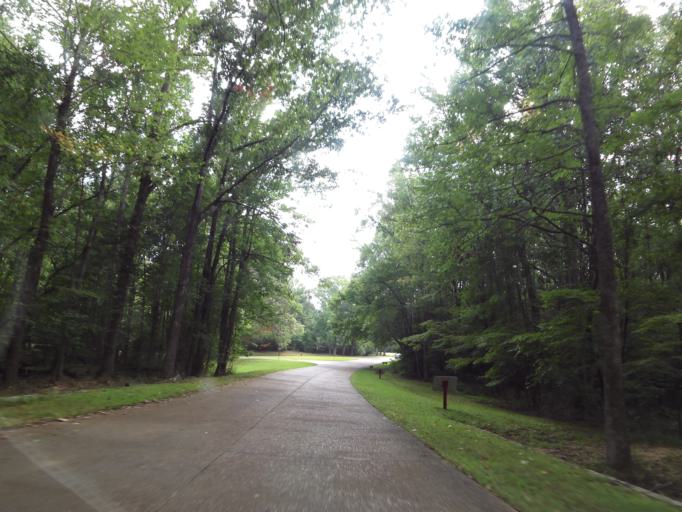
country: US
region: Tennessee
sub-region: Hardin County
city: Crump
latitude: 35.1310
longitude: -88.3559
